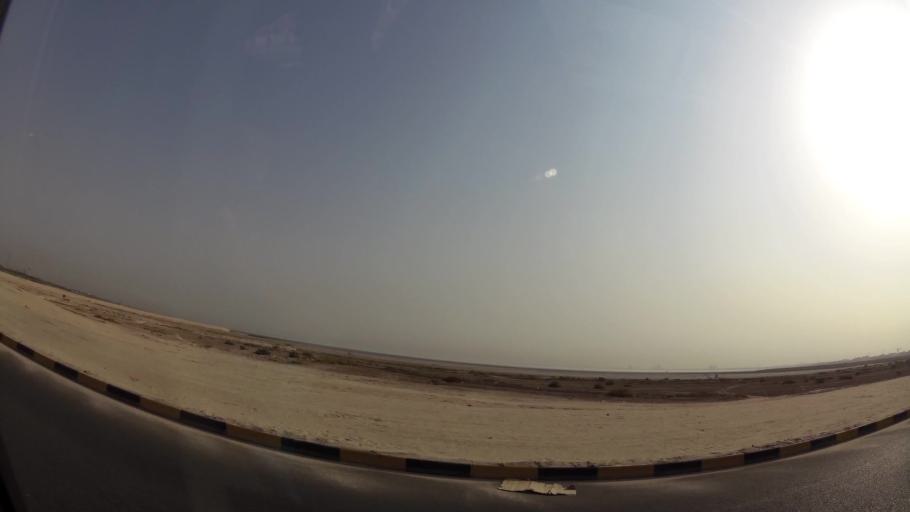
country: KW
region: Al Asimah
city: Ar Rabiyah
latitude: 29.3280
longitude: 47.8170
